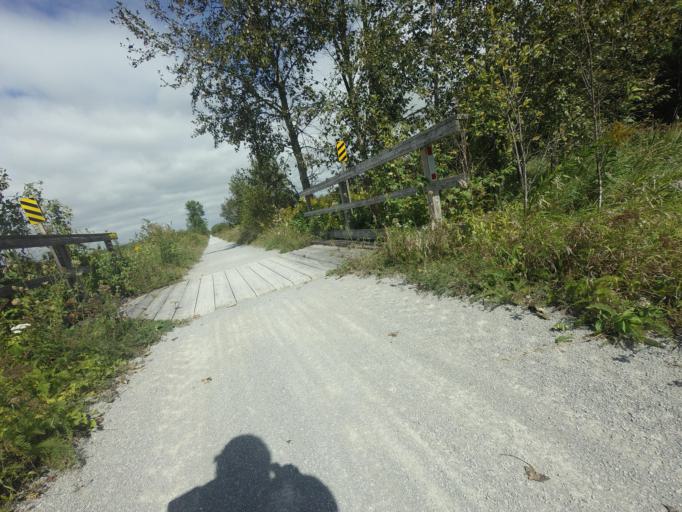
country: CA
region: Ontario
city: Uxbridge
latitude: 44.1855
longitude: -79.0683
